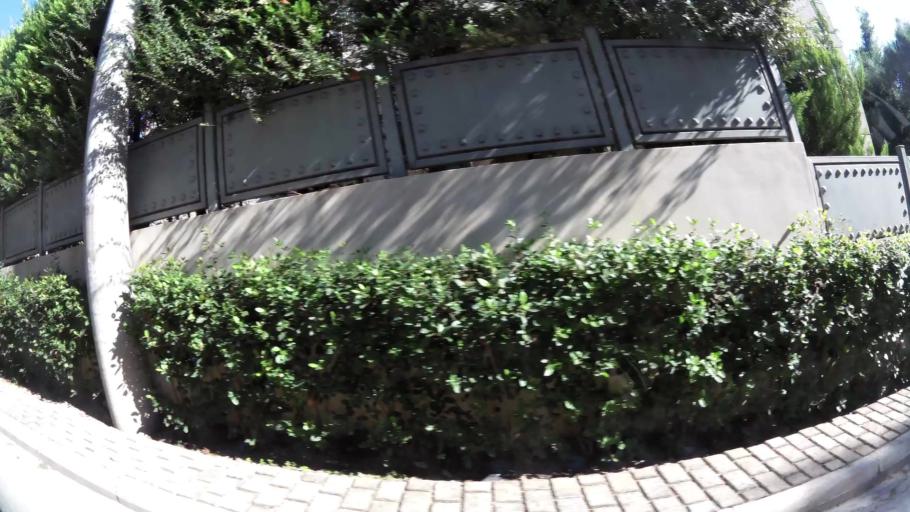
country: GR
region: Attica
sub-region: Nomarchia Athinas
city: Ekali
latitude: 38.1193
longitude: 23.8418
